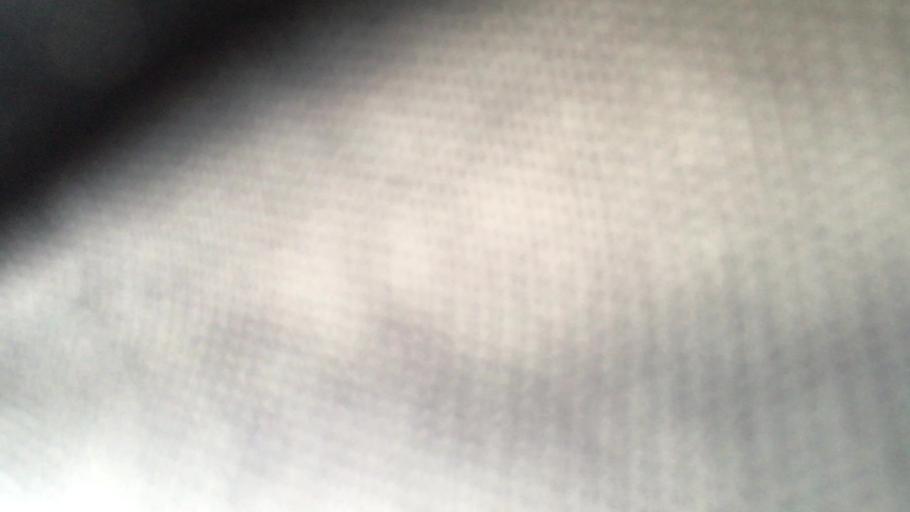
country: US
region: Maryland
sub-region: Somerset County
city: Princess Anne
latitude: 38.1770
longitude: -75.6896
